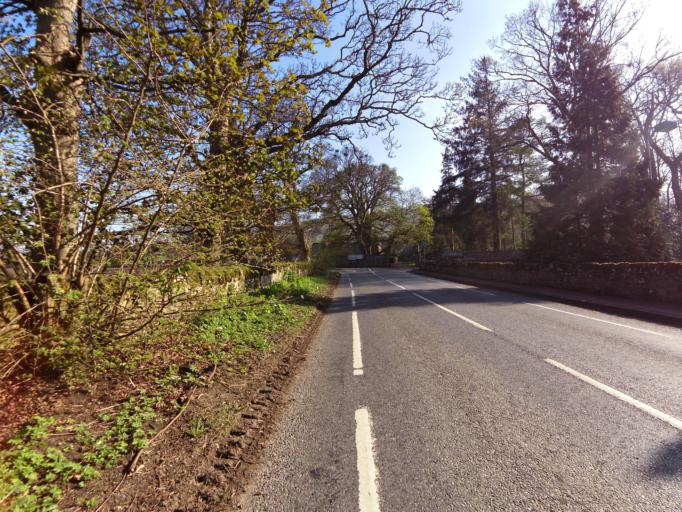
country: GB
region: Scotland
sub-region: Fife
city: Falkland
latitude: 56.2566
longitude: -3.2060
